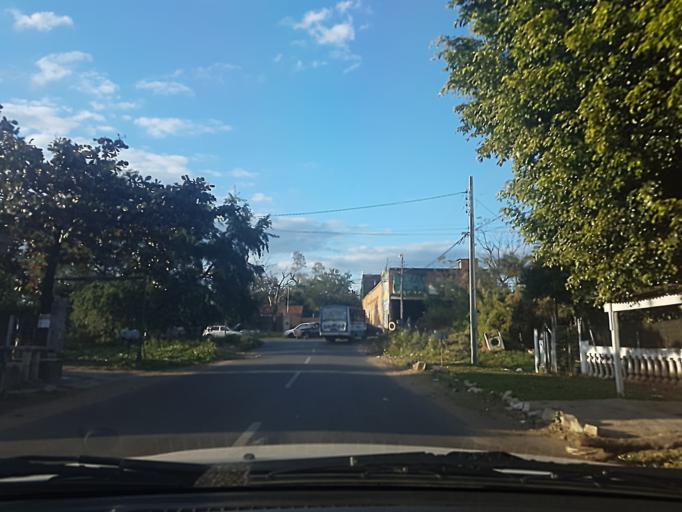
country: PY
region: Central
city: Colonia Mariano Roque Alonso
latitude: -25.2358
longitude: -57.5377
